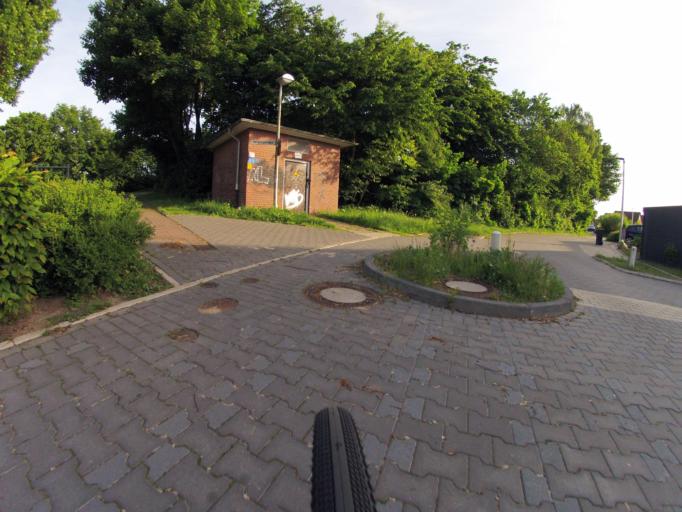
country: DE
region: North Rhine-Westphalia
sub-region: Regierungsbezirk Munster
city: Tecklenburg
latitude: 52.2600
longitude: 7.7813
